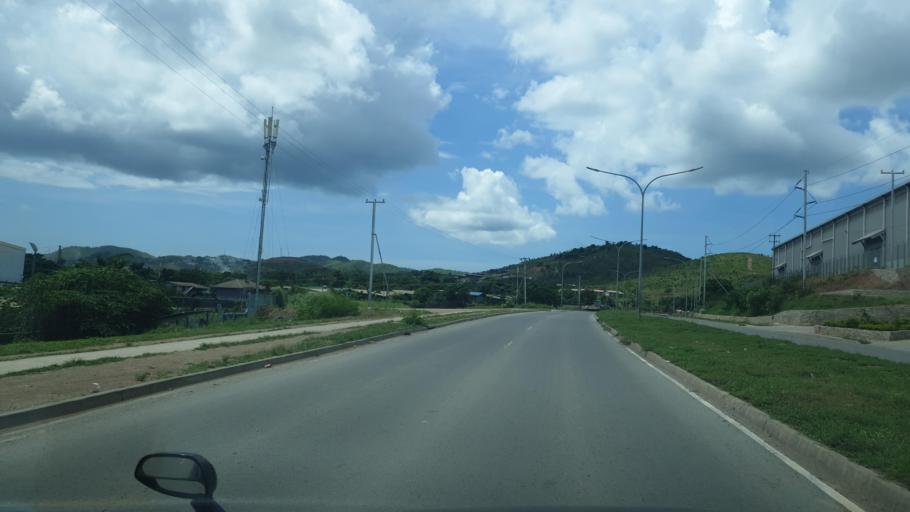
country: PG
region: National Capital
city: Port Moresby
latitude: -9.3861
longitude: 147.1549
